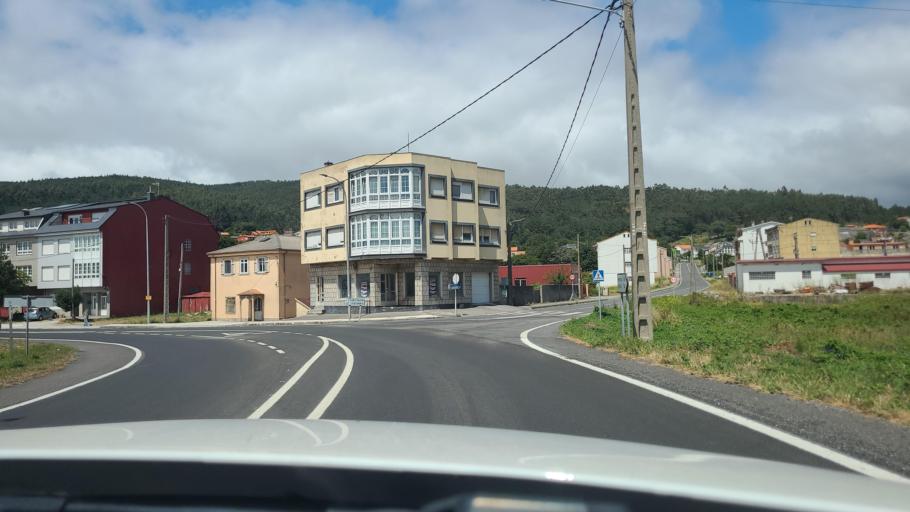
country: ES
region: Galicia
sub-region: Provincia da Coruna
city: Cee
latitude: 42.9464
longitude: -9.1710
